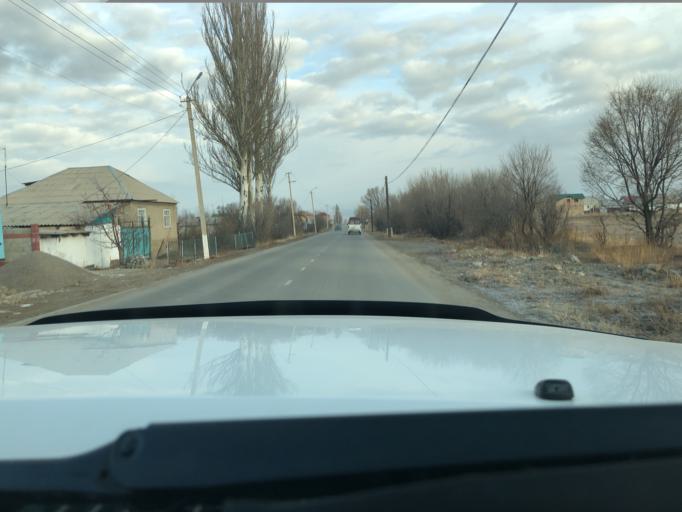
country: KG
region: Ysyk-Koel
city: Karakol
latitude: 42.4687
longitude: 78.3730
